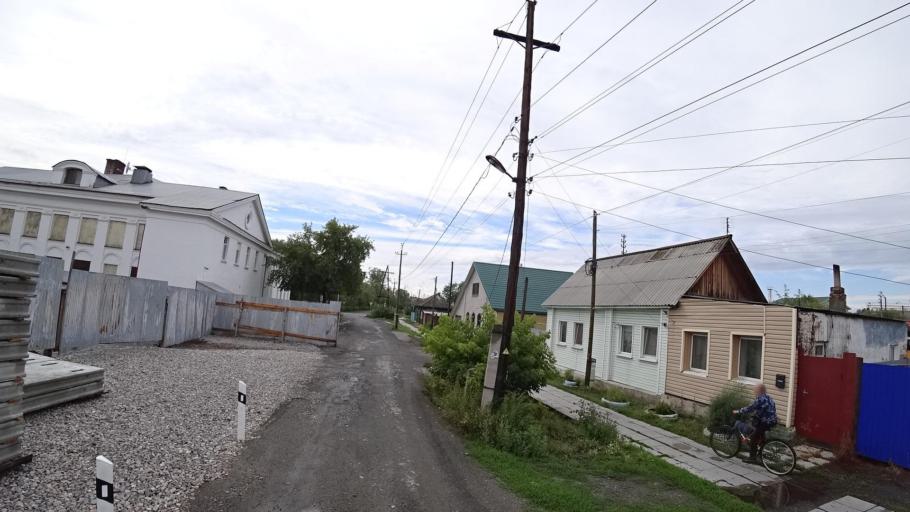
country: RU
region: Sverdlovsk
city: Kamyshlov
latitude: 56.8461
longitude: 62.7215
